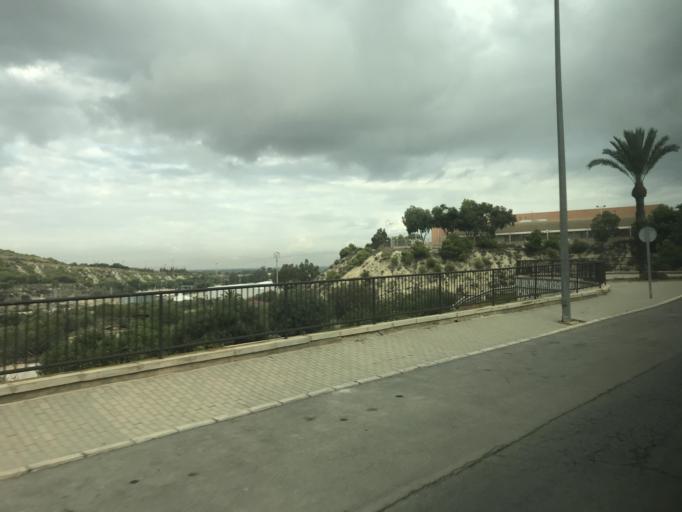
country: ES
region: Valencia
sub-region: Provincia de Alicante
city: Guardamar del Segura
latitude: 38.0850
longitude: -0.6554
